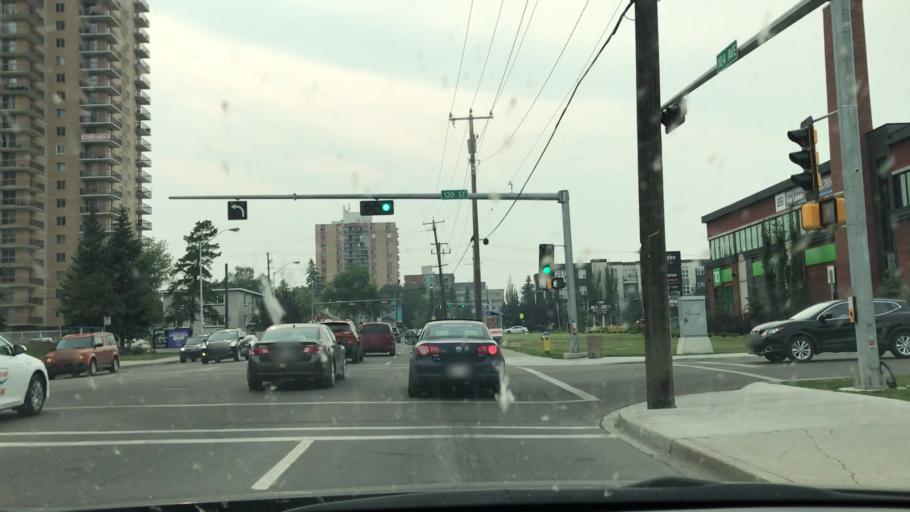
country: CA
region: Alberta
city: Edmonton
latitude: 53.5463
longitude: -113.5283
